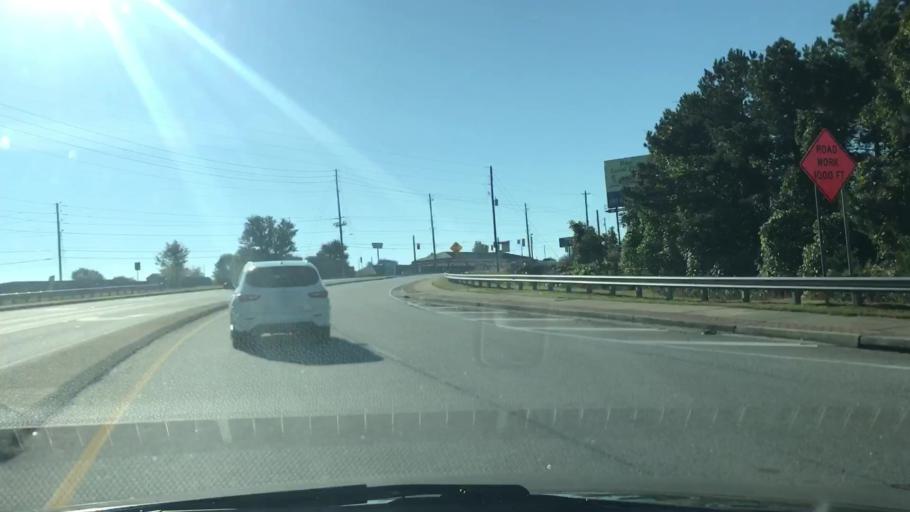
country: US
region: Georgia
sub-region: Douglas County
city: Douglasville
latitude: 33.7319
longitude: -84.7629
